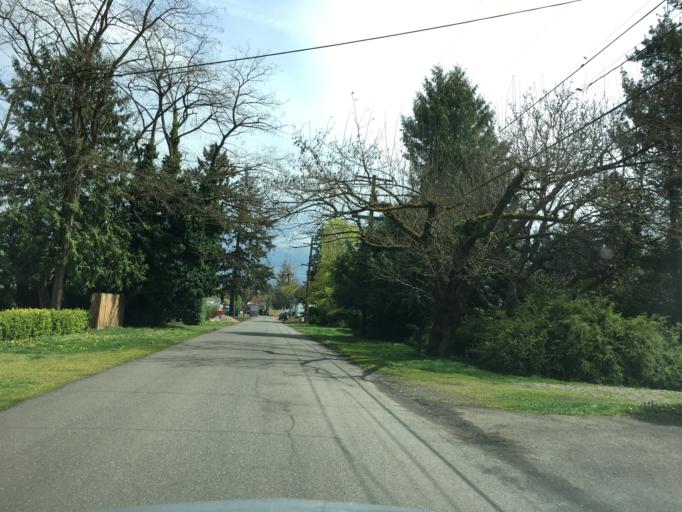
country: US
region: Oregon
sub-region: Multnomah County
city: Lents
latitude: 45.5582
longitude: -122.5910
